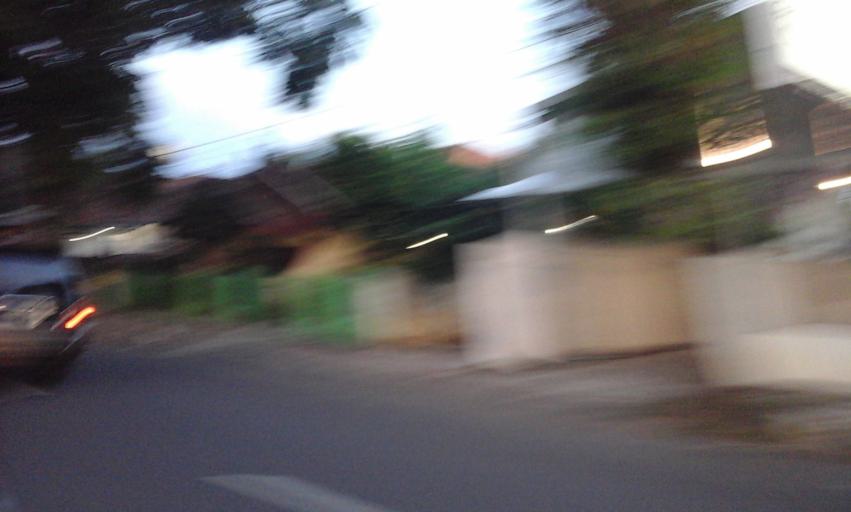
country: ID
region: East Java
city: Kepatihan
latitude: -8.1742
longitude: 113.7007
